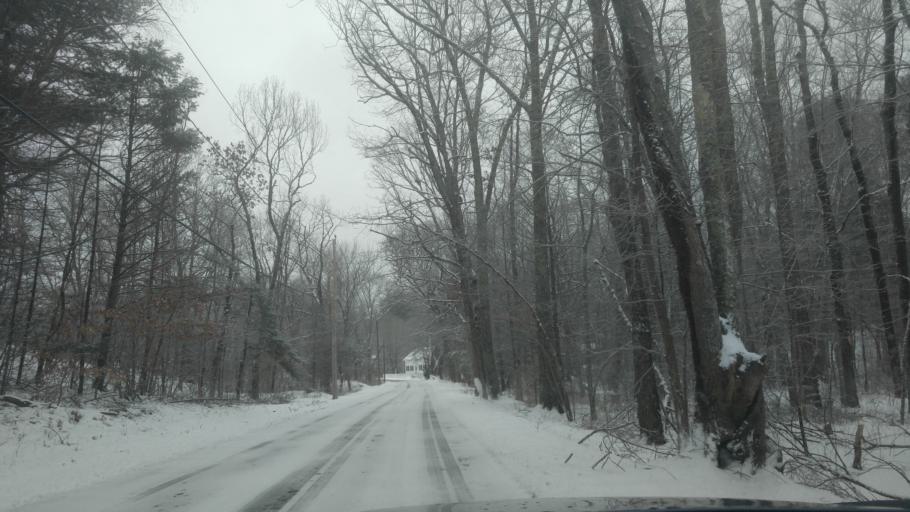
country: US
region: Rhode Island
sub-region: Providence County
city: Foster
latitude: 41.8283
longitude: -71.7482
